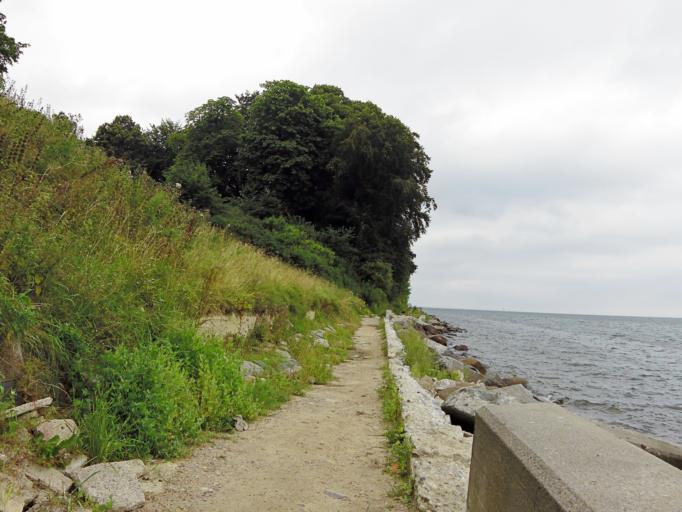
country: DK
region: Capital Region
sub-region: Gentofte Kommune
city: Charlottenlund
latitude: 55.8023
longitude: 12.5877
